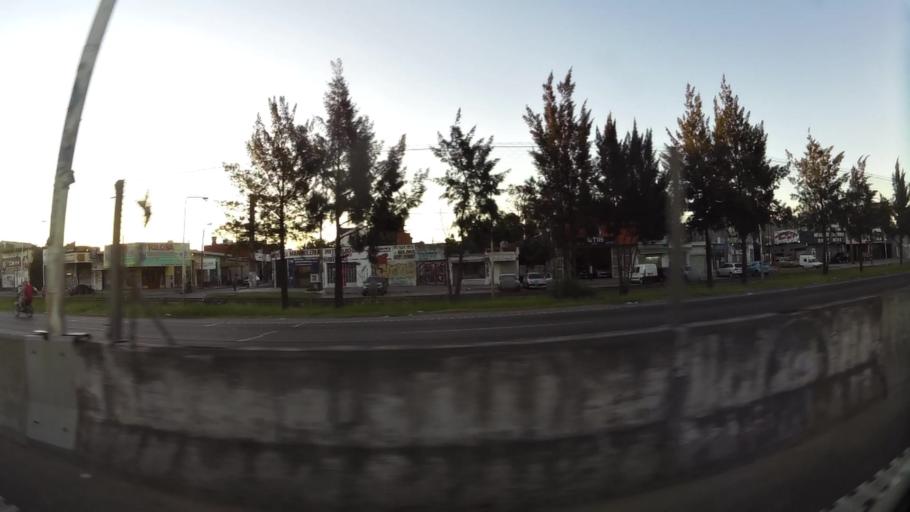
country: AR
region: Buenos Aires
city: Pontevedra
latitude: -34.7706
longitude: -58.6198
